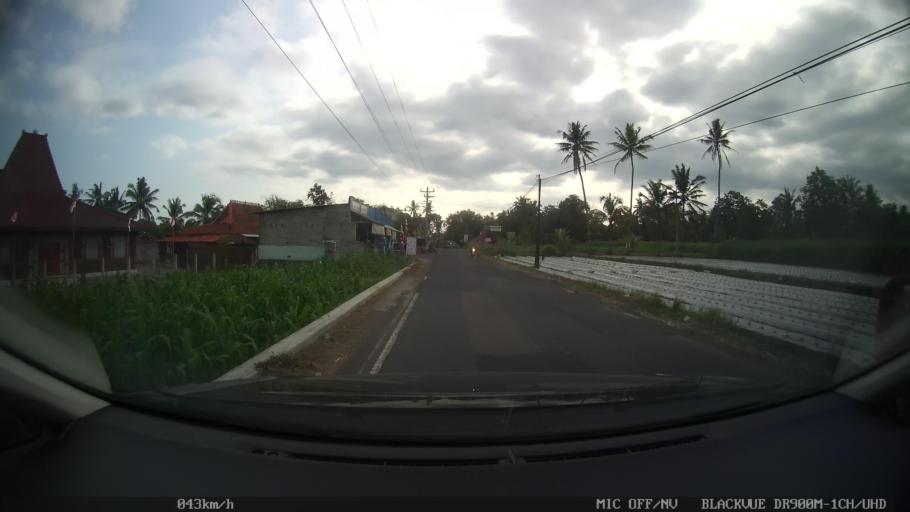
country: ID
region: Daerah Istimewa Yogyakarta
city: Depok
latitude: -7.6824
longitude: 110.4413
